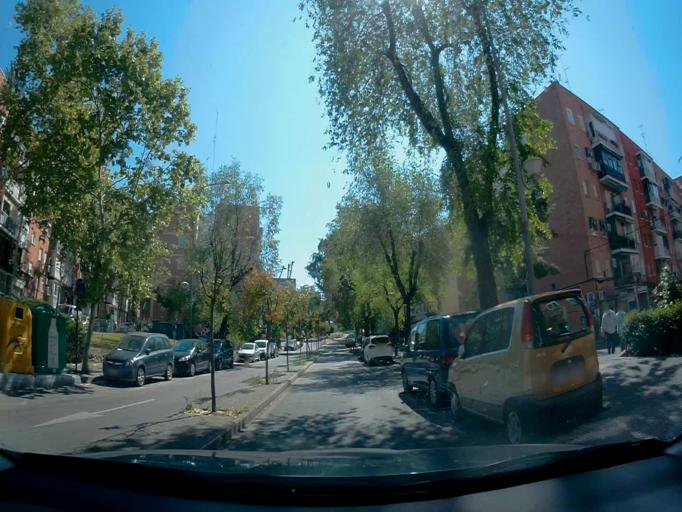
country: ES
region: Madrid
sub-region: Provincia de Madrid
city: Alcorcon
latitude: 40.3431
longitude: -3.8308
